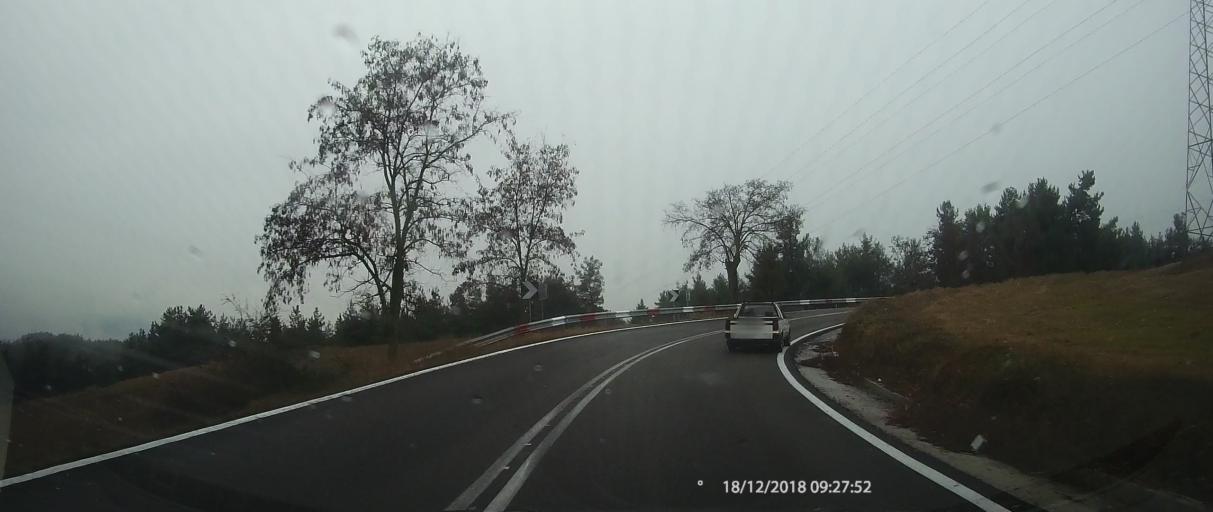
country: GR
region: Thessaly
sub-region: Nomos Larisis
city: Elassona
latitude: 39.9177
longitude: 22.1736
